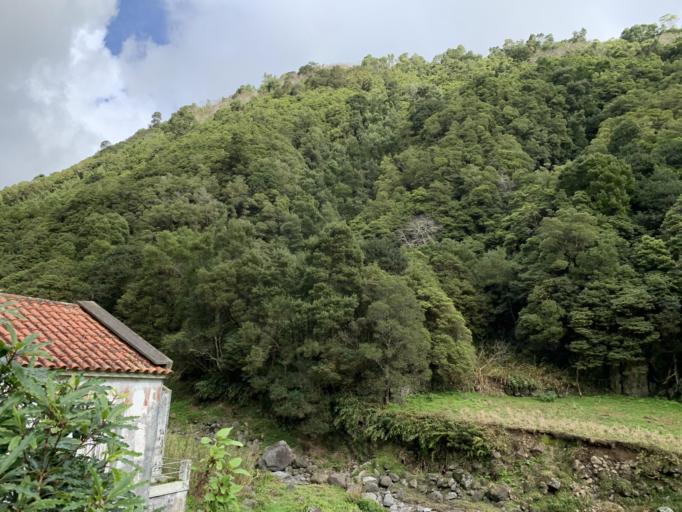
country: PT
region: Azores
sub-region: Povoacao
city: Furnas
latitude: 37.7502
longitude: -25.2023
